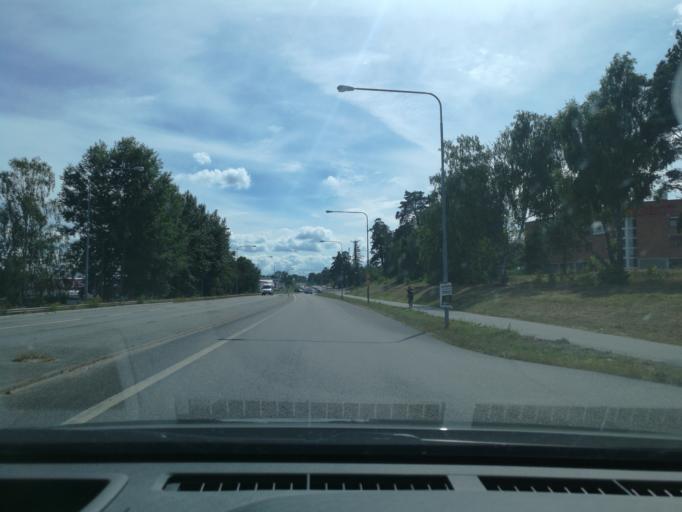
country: SE
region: Stockholm
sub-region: Upplands Vasby Kommun
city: Upplands Vaesby
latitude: 59.5034
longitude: 17.9231
